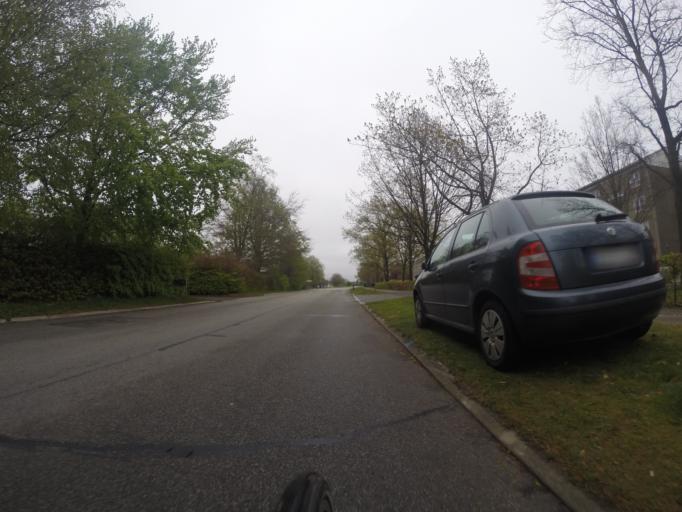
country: DK
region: Capital Region
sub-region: Herlev Kommune
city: Herlev
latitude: 55.7441
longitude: 12.4315
